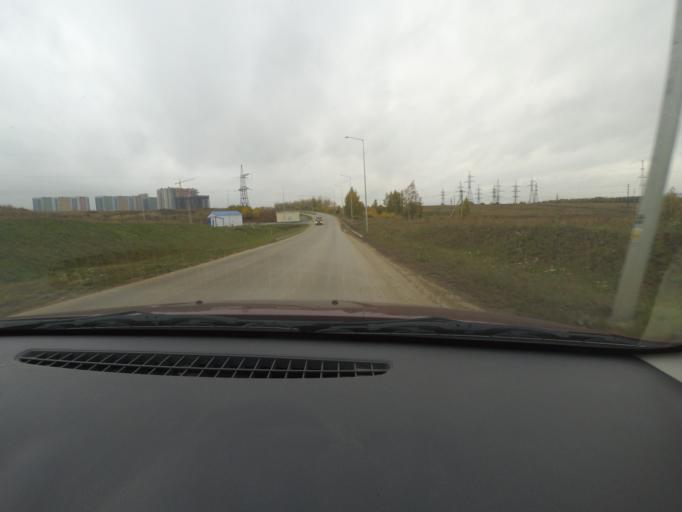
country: RU
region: Nizjnij Novgorod
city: Afonino
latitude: 56.2446
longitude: 44.0589
